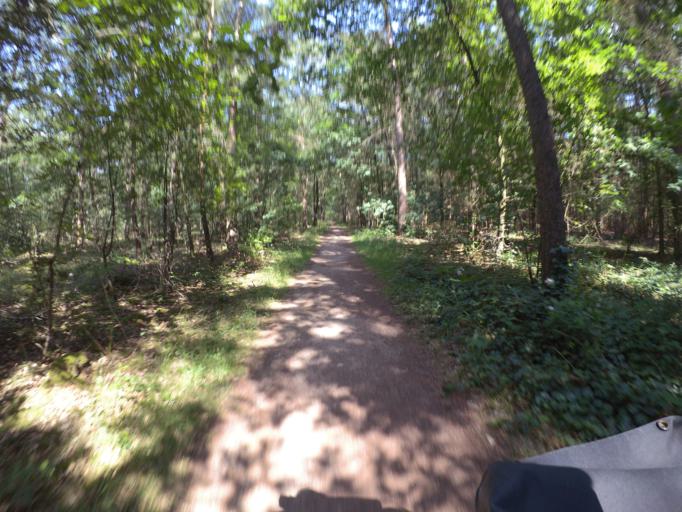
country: NL
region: North Brabant
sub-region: Gemeente Maasdonk
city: Geffen
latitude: 51.7040
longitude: 5.4058
